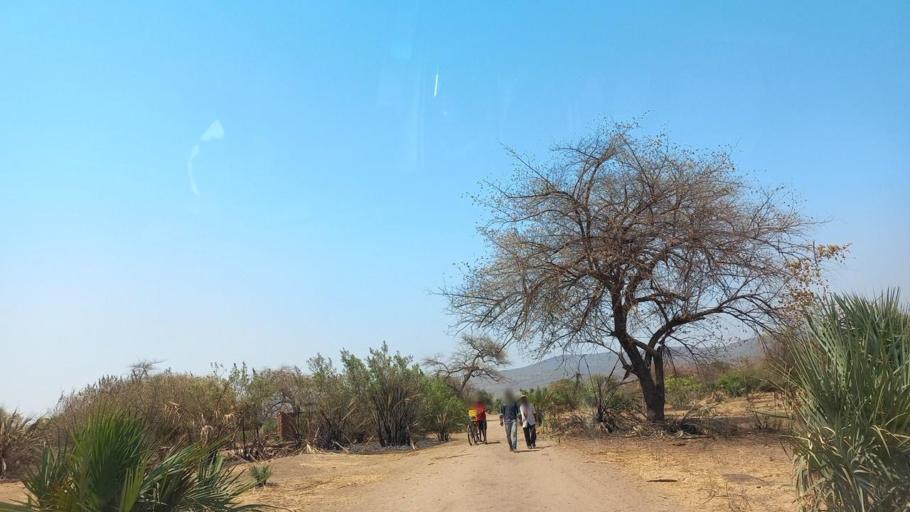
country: ZM
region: Lusaka
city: Luangwa
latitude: -15.1953
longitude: 30.1921
